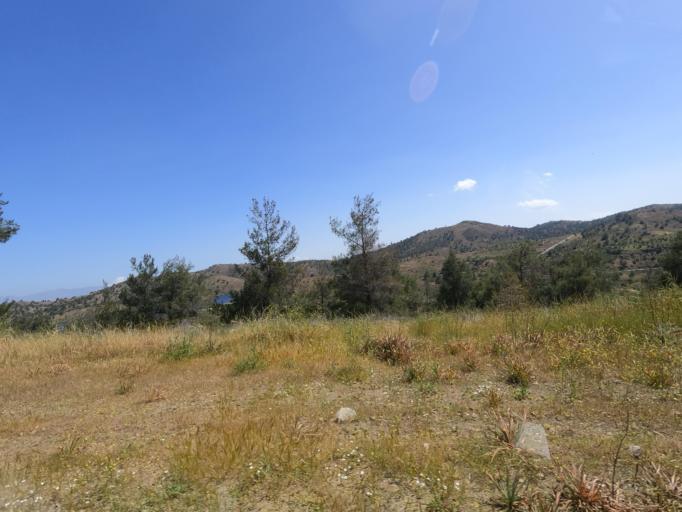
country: CY
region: Lefkosia
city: Astromeritis
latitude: 35.0562
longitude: 33.0240
